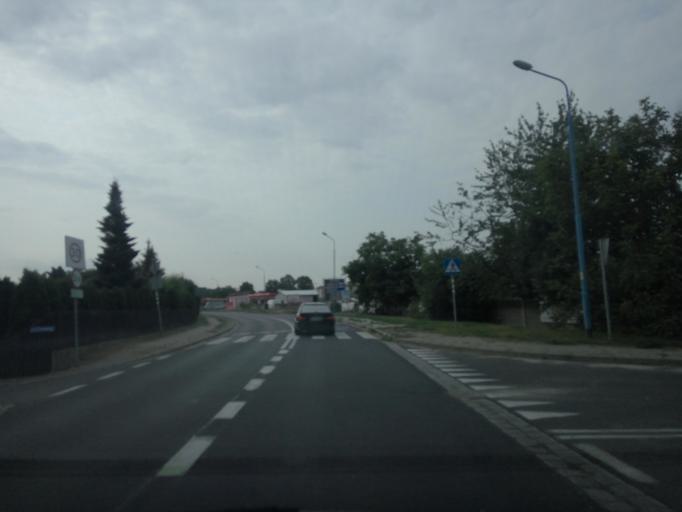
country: PL
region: Lower Silesian Voivodeship
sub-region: Powiat strzelinski
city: Strzelin
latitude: 50.7924
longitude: 17.0657
